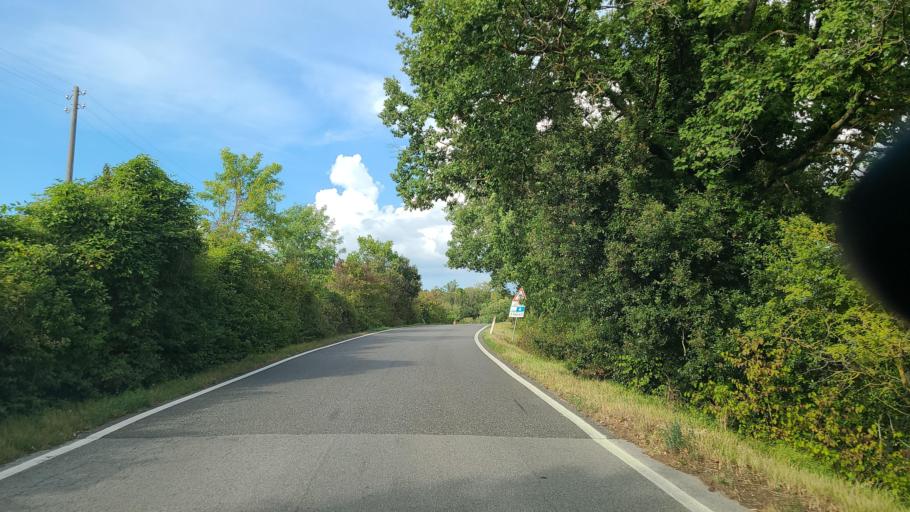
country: IT
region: Tuscany
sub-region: Province of Florence
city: Gambassi Terme
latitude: 43.4758
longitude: 10.9529
